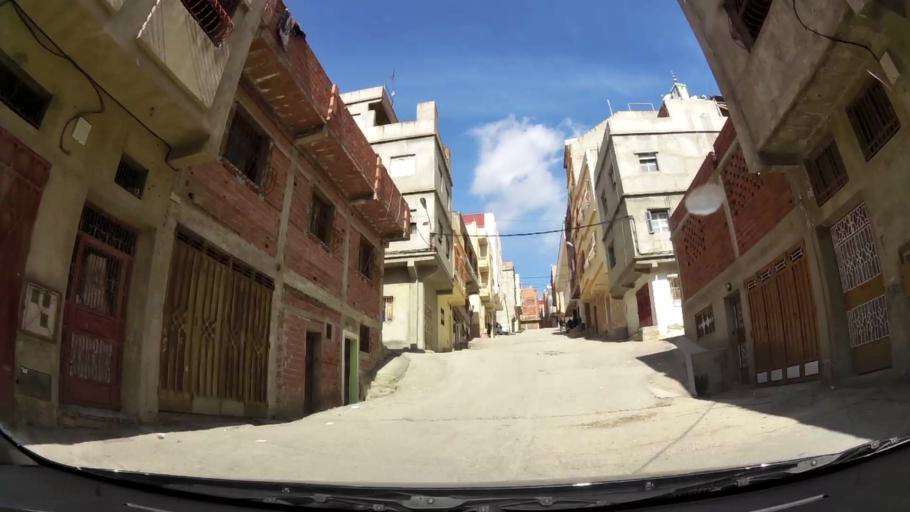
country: MA
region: Tanger-Tetouan
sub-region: Tanger-Assilah
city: Tangier
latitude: 35.7671
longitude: -5.7702
